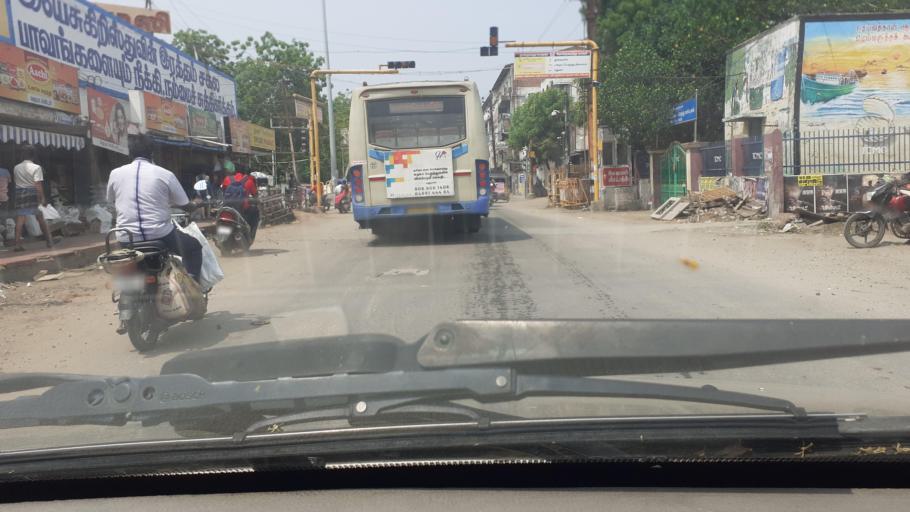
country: IN
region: Tamil Nadu
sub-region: Thoothukkudi
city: Korampallam
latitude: 8.8020
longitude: 78.1387
